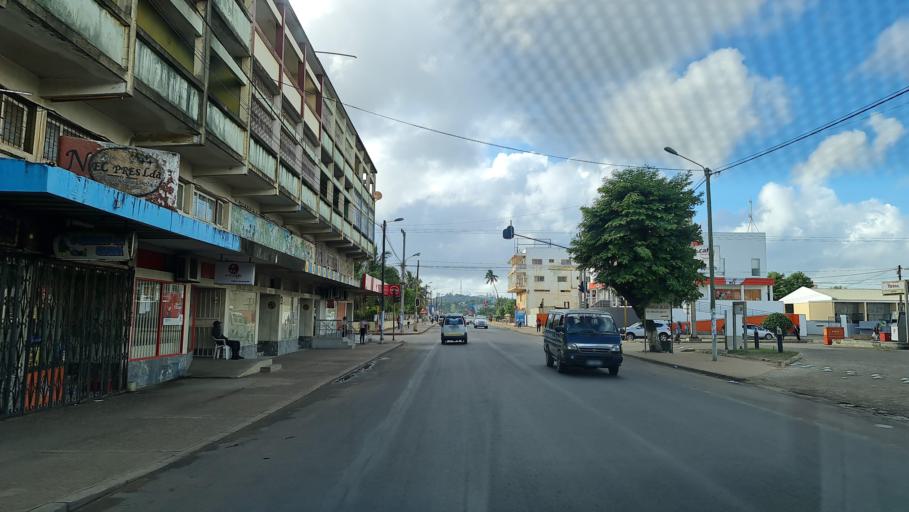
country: MZ
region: Gaza
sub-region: Xai-Xai District
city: Xai-Xai
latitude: -25.0459
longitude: 33.6440
